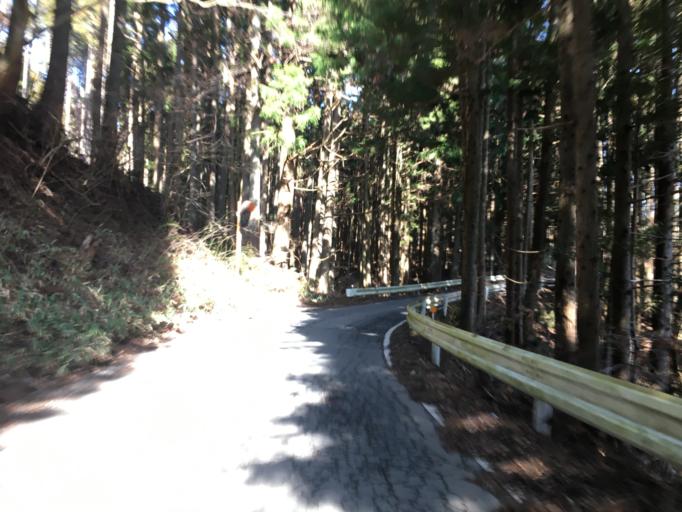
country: JP
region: Ibaraki
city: Takahagi
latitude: 36.8274
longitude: 140.5482
